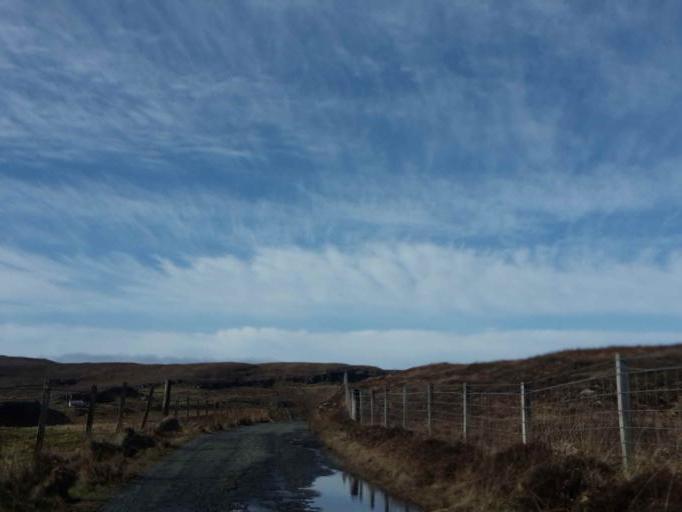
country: GB
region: Scotland
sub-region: Eilean Siar
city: Harris
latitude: 57.4539
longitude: -6.7188
